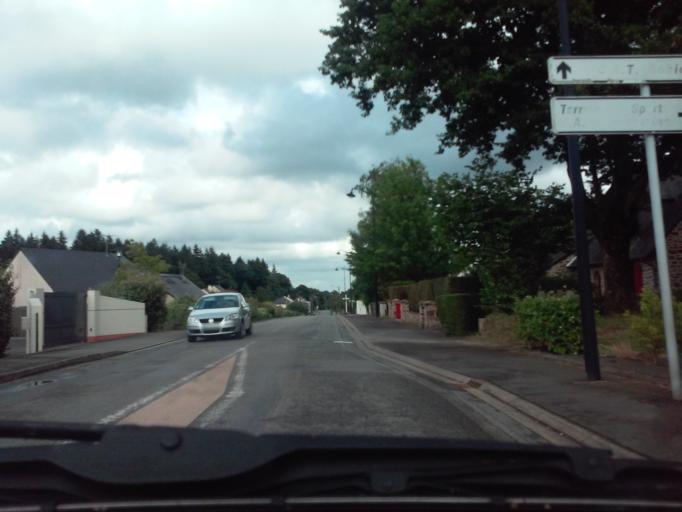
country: FR
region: Pays de la Loire
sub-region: Departement de la Mayenne
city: Port-Brillet
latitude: 48.1149
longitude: -0.9655
